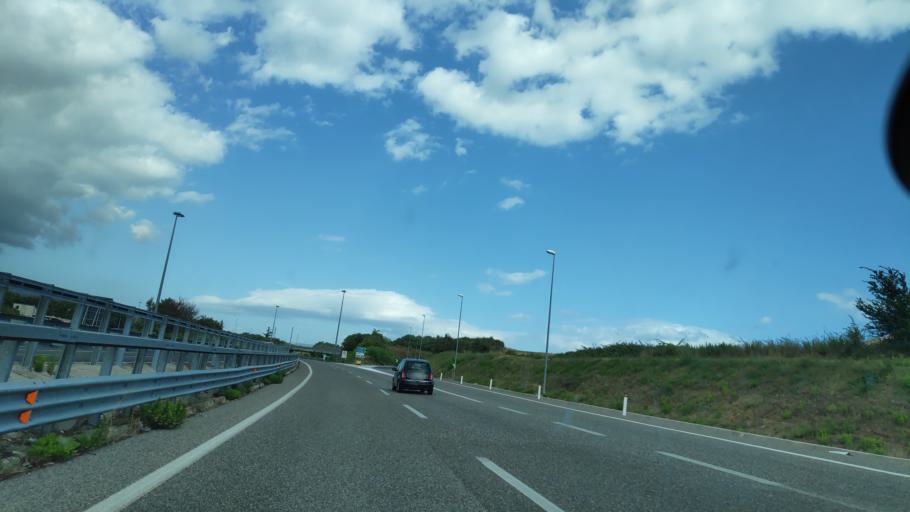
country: IT
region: Campania
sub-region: Provincia di Salerno
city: Palomonte
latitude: 40.6101
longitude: 15.2884
